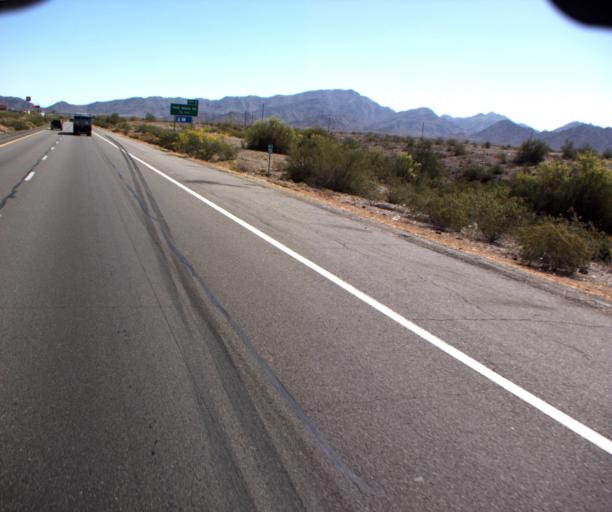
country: US
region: Arizona
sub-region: La Paz County
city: Ehrenberg
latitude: 33.6201
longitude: -114.4483
